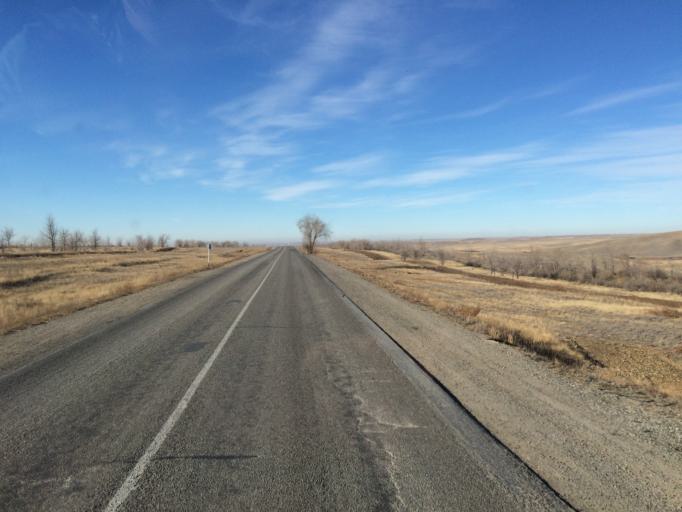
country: KZ
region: Aqtoebe
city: Aqtobe
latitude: 50.2828
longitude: 57.7418
